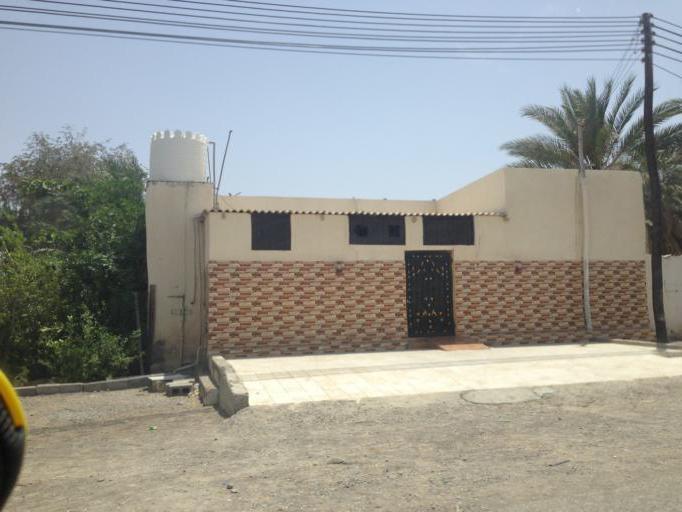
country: OM
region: Muhafazat Masqat
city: As Sib al Jadidah
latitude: 23.6870
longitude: 58.1139
